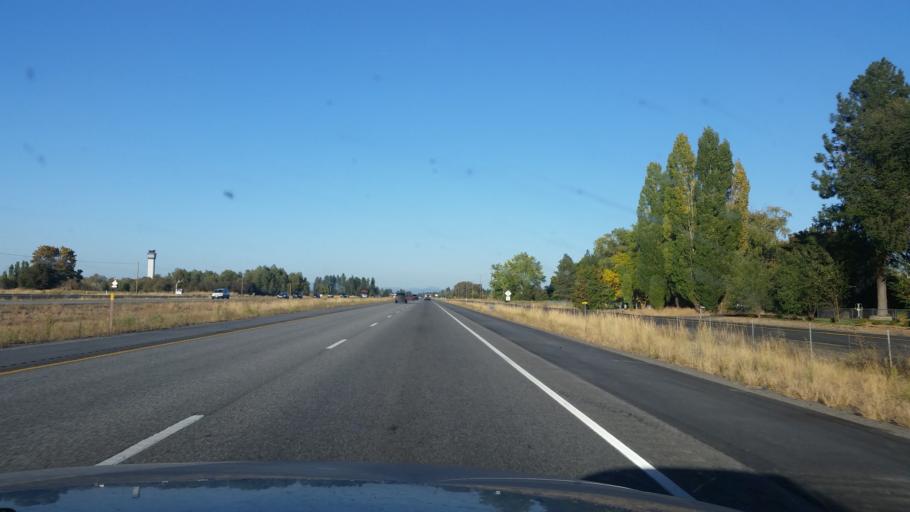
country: US
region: Washington
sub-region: Spokane County
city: Airway Heights
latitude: 47.6033
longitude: -117.5394
